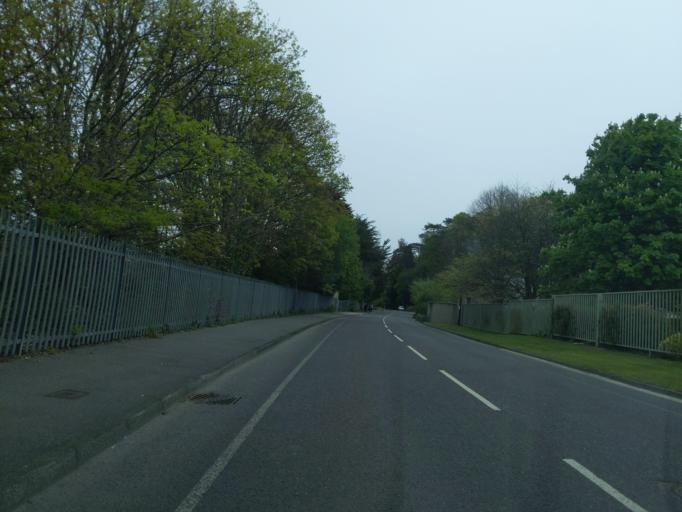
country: GB
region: England
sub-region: Cornwall
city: Par
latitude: 50.3556
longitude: -4.7117
